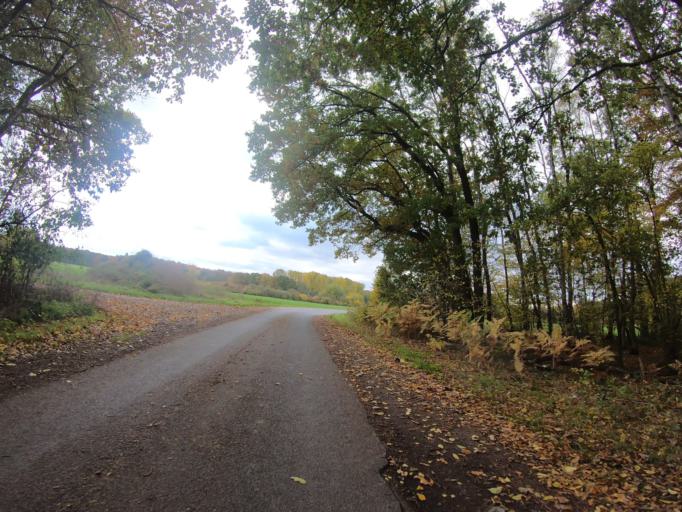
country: DE
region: Lower Saxony
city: Ribbesbuttel
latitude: 52.4127
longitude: 10.4807
